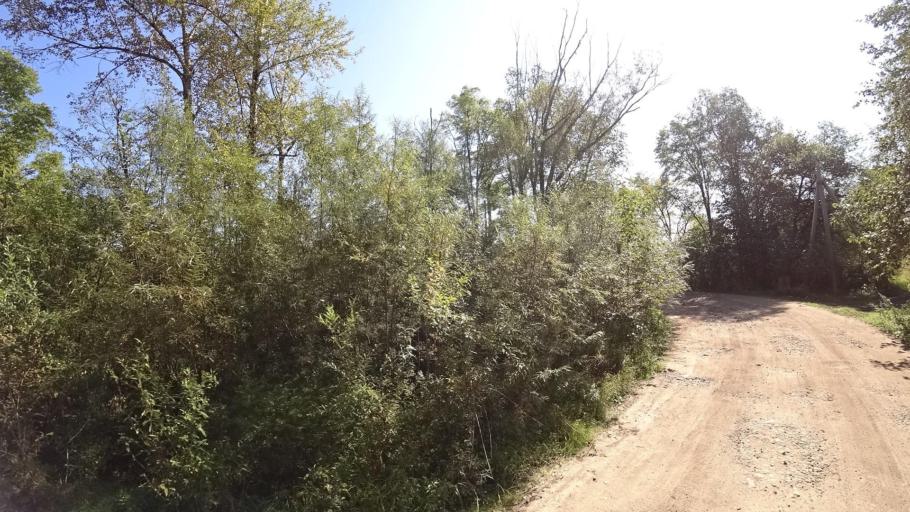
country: RU
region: Jewish Autonomous Oblast
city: Bira
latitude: 49.0021
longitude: 132.4478
